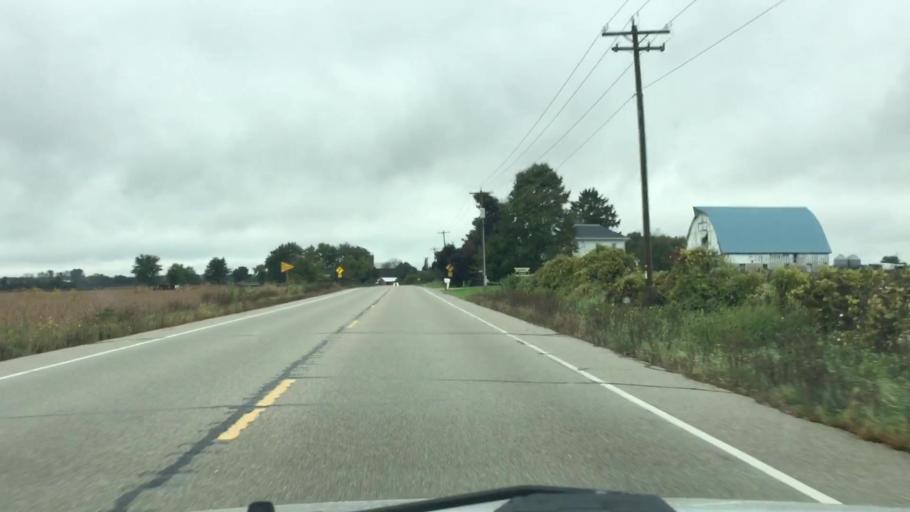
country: US
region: Wisconsin
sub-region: Walworth County
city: Whitewater
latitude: 42.8091
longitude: -88.7628
